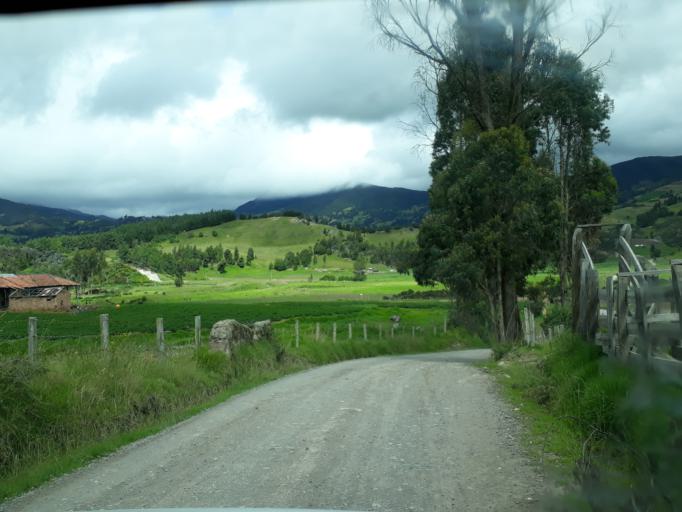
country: CO
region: Cundinamarca
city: Carmen de Carupa
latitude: 5.3067
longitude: -73.9006
